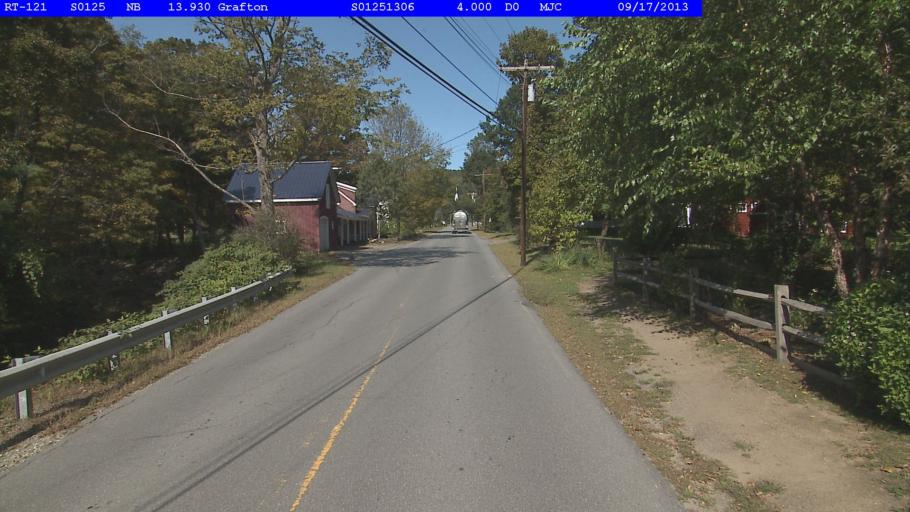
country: US
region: Vermont
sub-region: Windsor County
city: Chester
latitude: 43.1701
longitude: -72.6040
